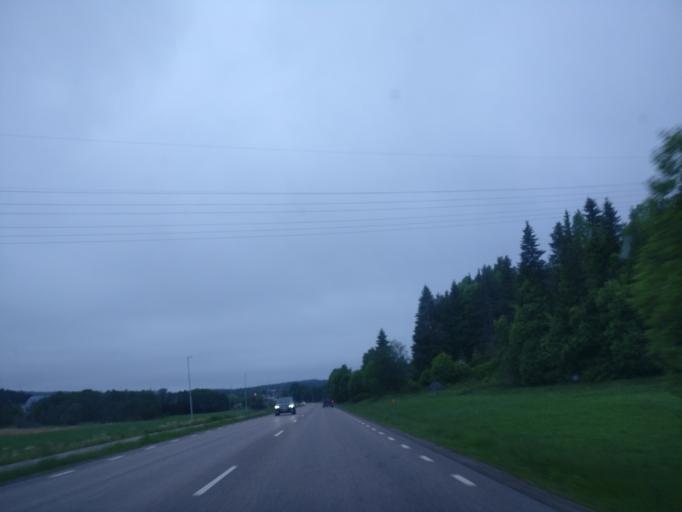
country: SE
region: Vaesternorrland
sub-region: Sundsvalls Kommun
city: Johannedal
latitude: 62.4131
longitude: 17.3639
